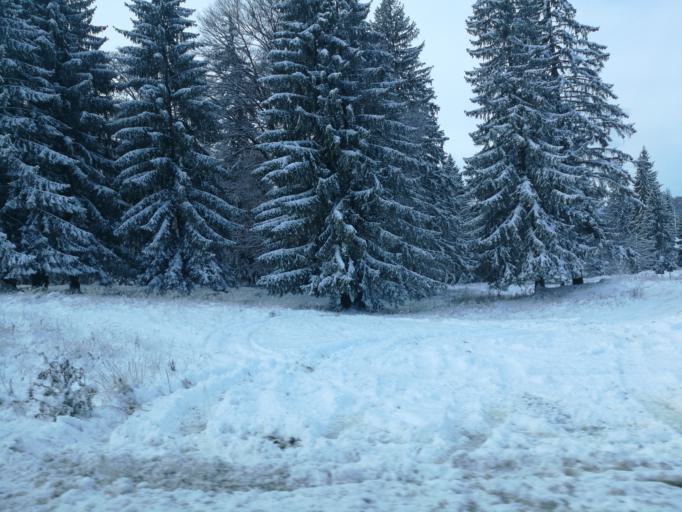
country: RO
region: Brasov
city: Brasov
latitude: 45.6076
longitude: 25.5544
